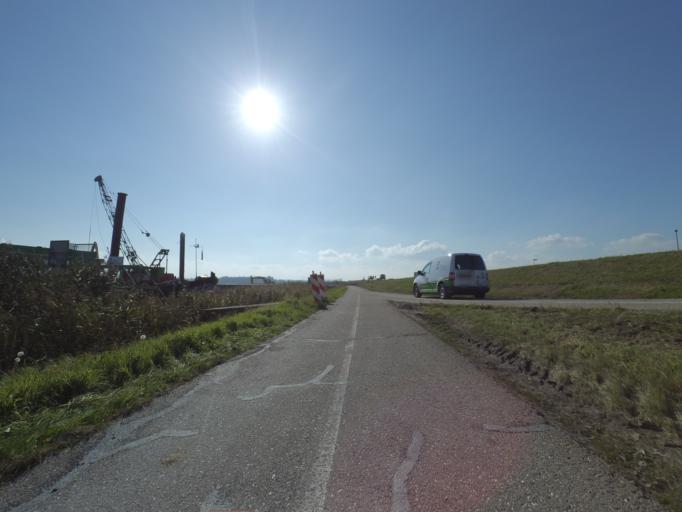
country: NL
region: Flevoland
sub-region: Gemeente Zeewolde
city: Zeewolde
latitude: 52.3506
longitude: 5.5386
